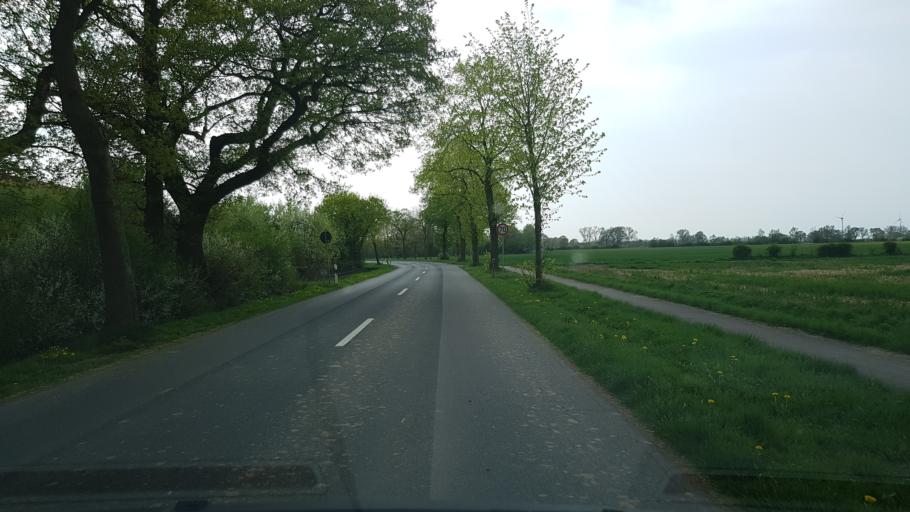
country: DE
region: Lower Saxony
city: Ahsen-Oetzen
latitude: 52.9557
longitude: 9.0631
